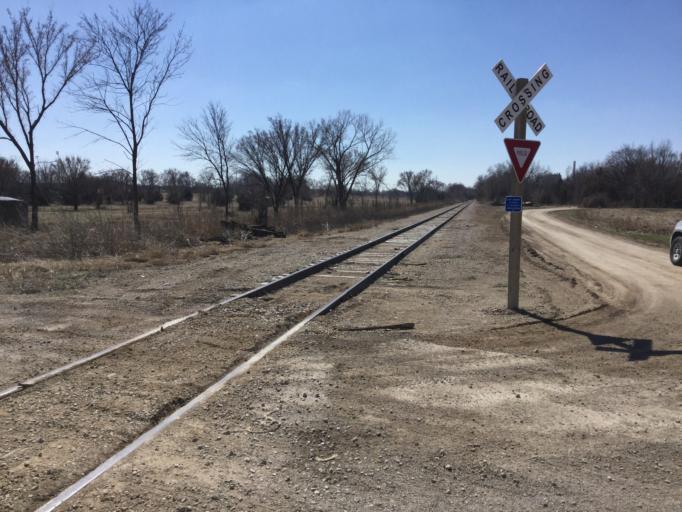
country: US
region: Kansas
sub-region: Allen County
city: Humboldt
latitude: 37.8108
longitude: -95.4286
